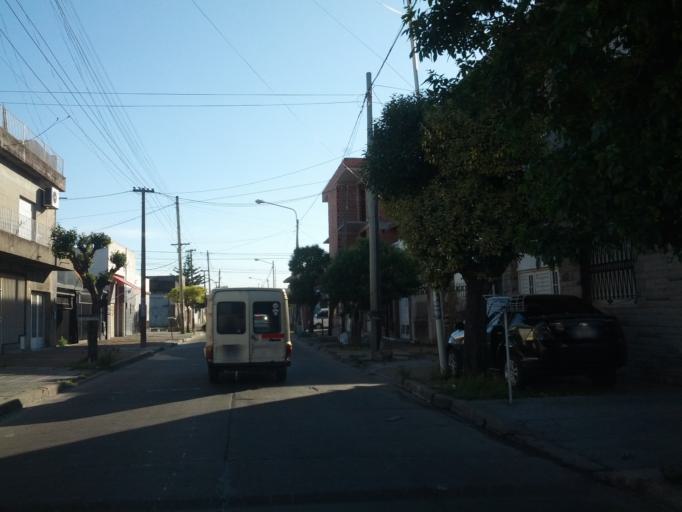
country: AR
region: Buenos Aires
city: San Justo
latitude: -34.6600
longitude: -58.5292
